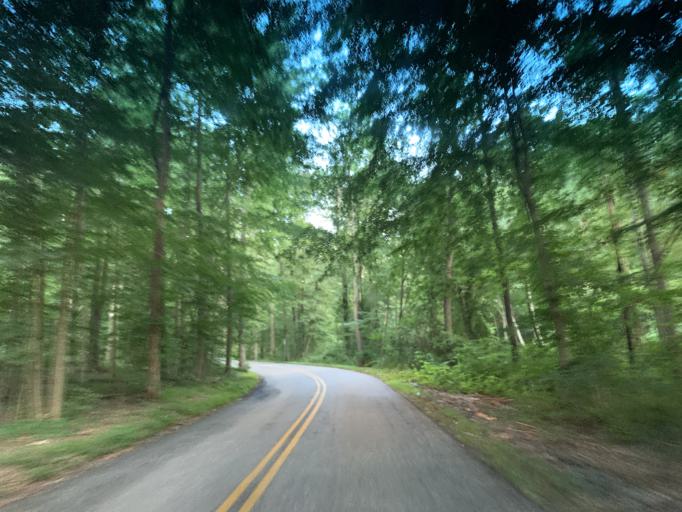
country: US
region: Maryland
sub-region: Harford County
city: Aberdeen
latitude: 39.5349
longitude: -76.1621
